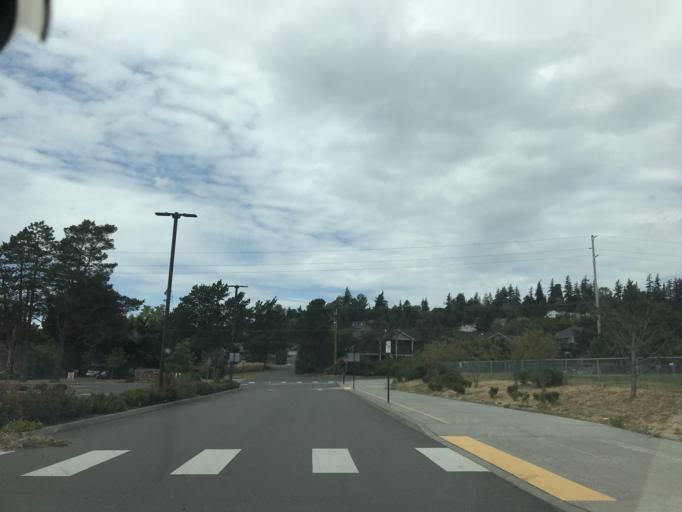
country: US
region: Washington
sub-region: Whatcom County
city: Bellingham
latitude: 48.7223
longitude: -122.4852
